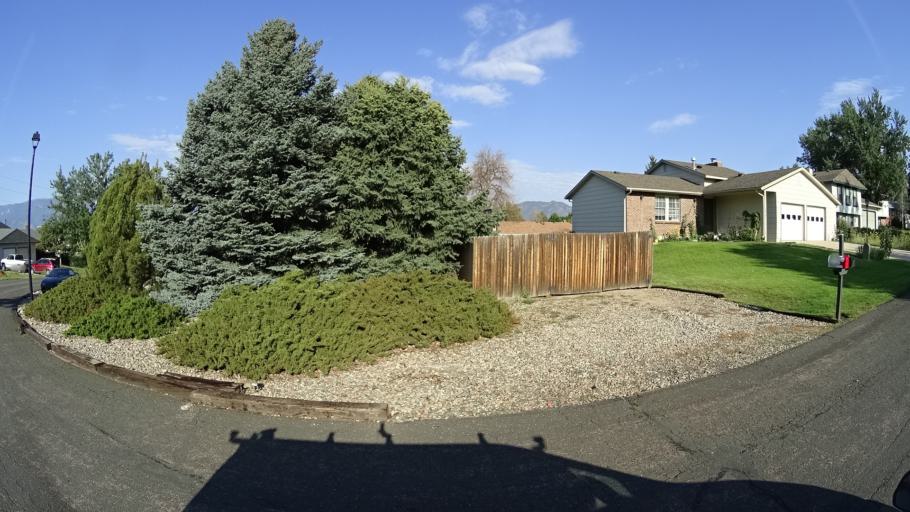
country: US
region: Colorado
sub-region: El Paso County
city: Air Force Academy
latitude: 38.9450
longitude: -104.7883
